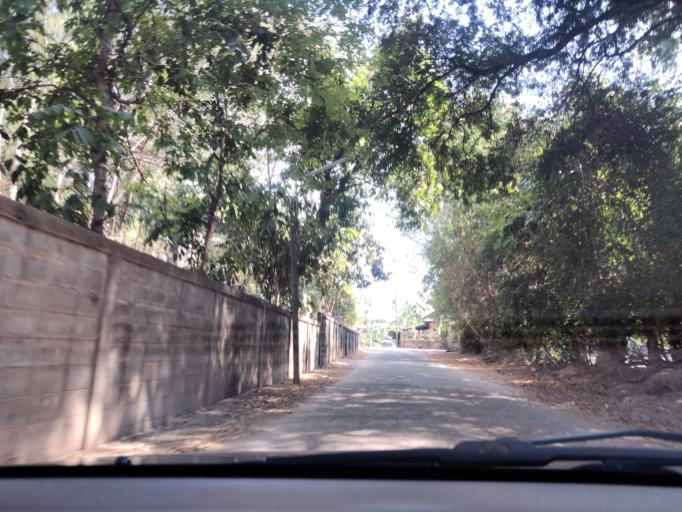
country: TH
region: Sisaket
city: Si Sa Ket
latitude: 15.0656
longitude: 104.3505
